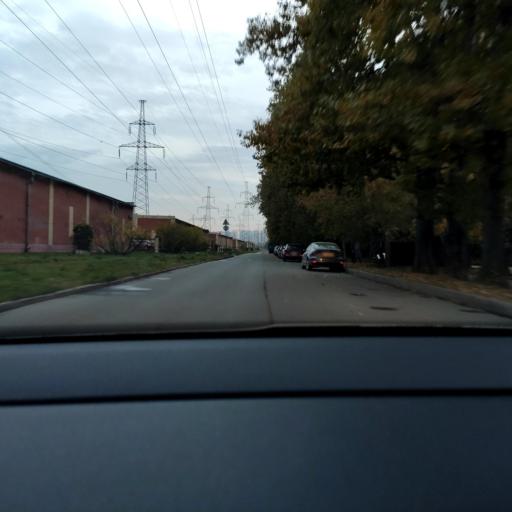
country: RU
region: Moscow
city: Bibirevo
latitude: 55.8876
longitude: 37.6187
